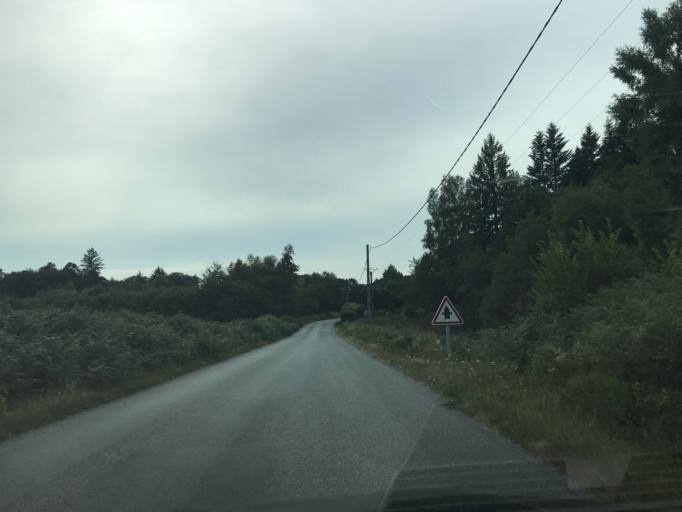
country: FR
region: Limousin
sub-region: Departement de la Correze
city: Neuvic
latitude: 45.3736
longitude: 2.2438
